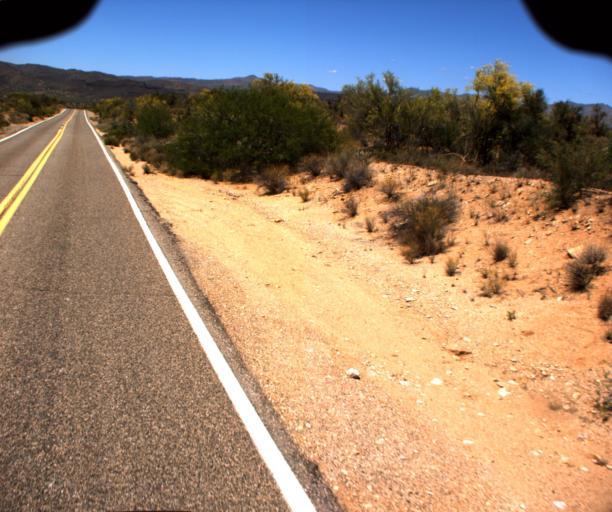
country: US
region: Arizona
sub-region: Yavapai County
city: Bagdad
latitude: 34.4671
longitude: -113.0474
